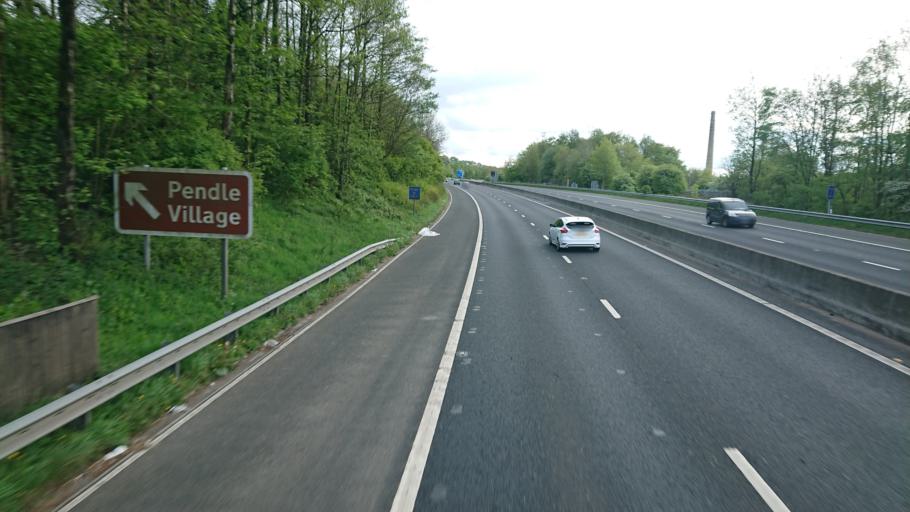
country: GB
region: England
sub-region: Lancashire
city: Barrowford
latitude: 53.8372
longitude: -2.2244
